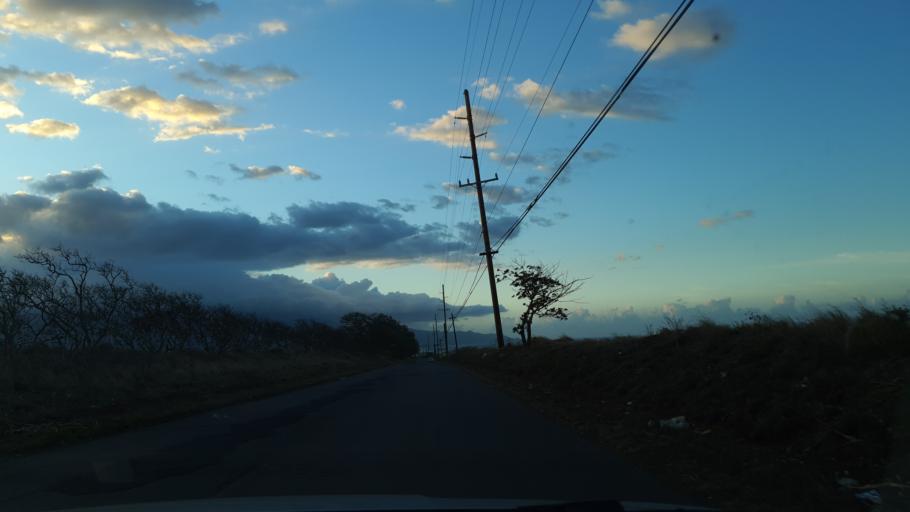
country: US
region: Hawaii
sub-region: Maui County
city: Kahului
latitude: 20.8614
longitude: -156.4275
